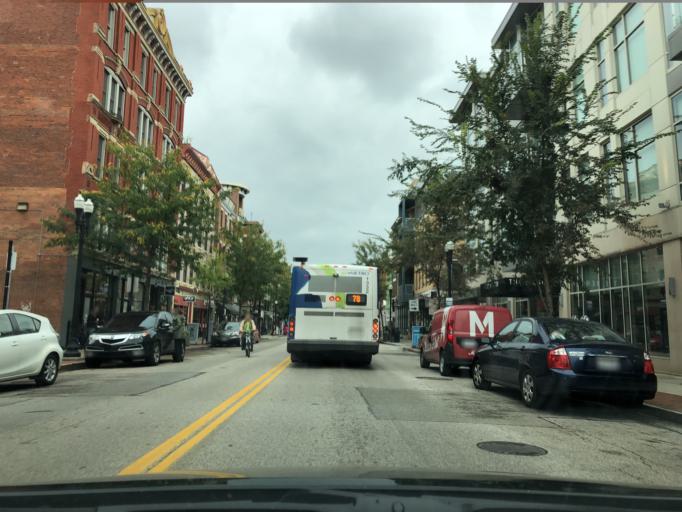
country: US
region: Kentucky
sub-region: Campbell County
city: Newport
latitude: 39.1098
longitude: -84.5152
